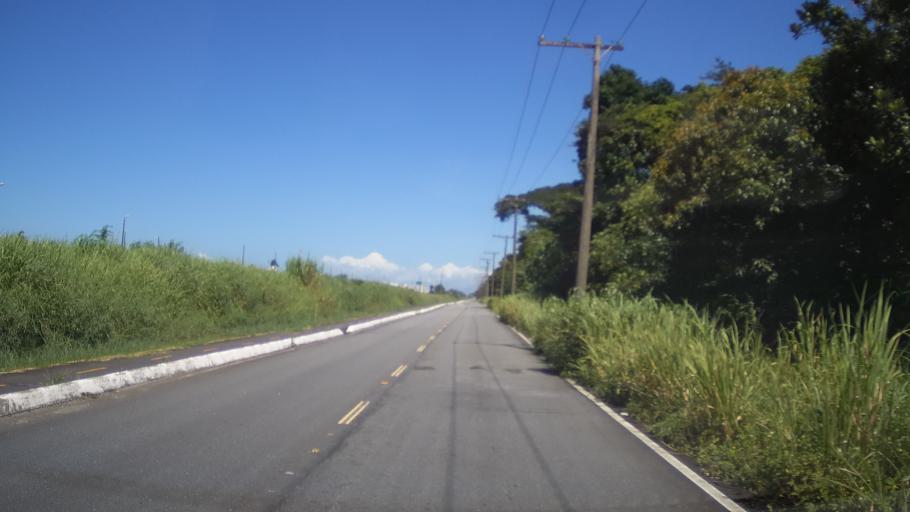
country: BR
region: Sao Paulo
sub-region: Mongagua
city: Mongagua
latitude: -24.0687
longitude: -46.5761
